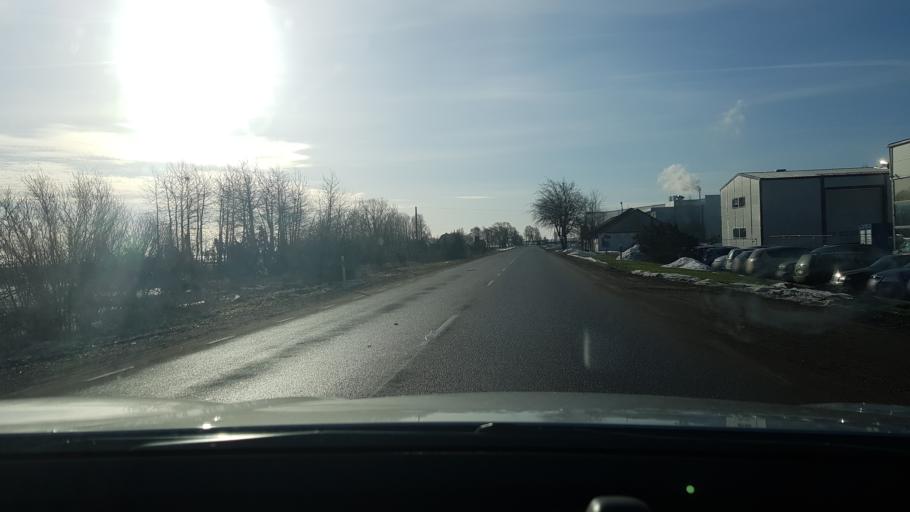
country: EE
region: Saare
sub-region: Kuressaare linn
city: Kuressaare
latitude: 58.2237
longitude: 22.5064
